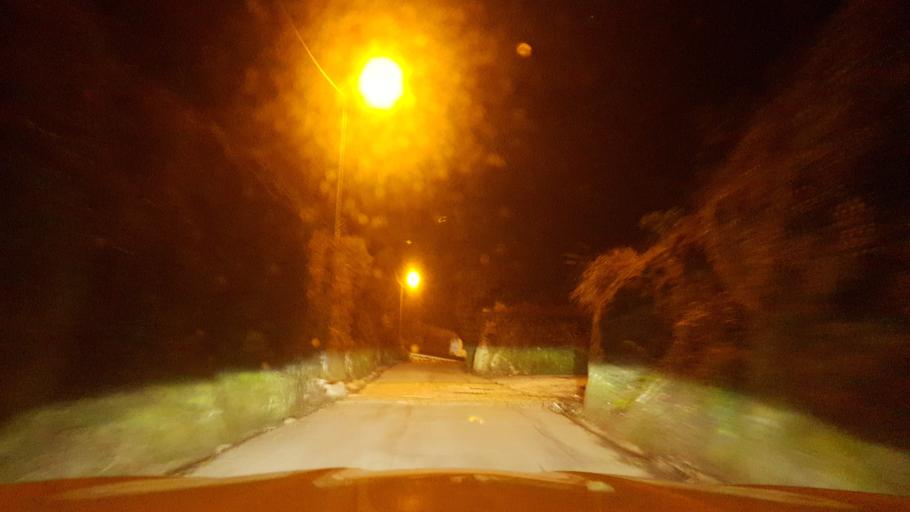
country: PT
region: Porto
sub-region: Matosinhos
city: Guifoes
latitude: 41.2120
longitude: -8.6427
